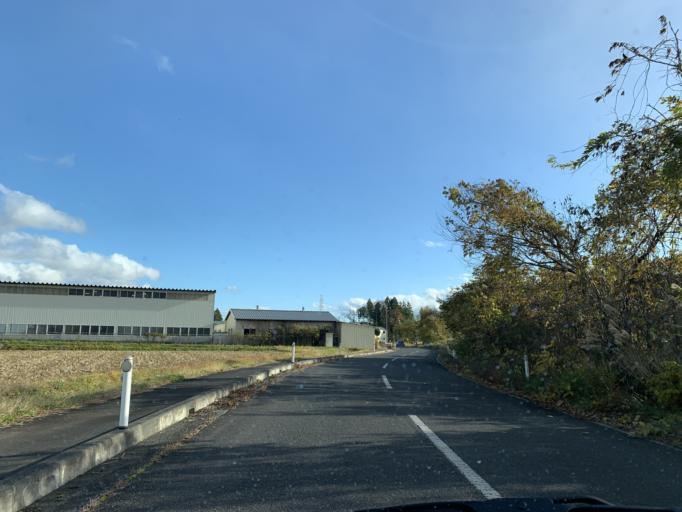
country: JP
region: Iwate
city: Mizusawa
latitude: 39.0279
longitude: 141.0764
